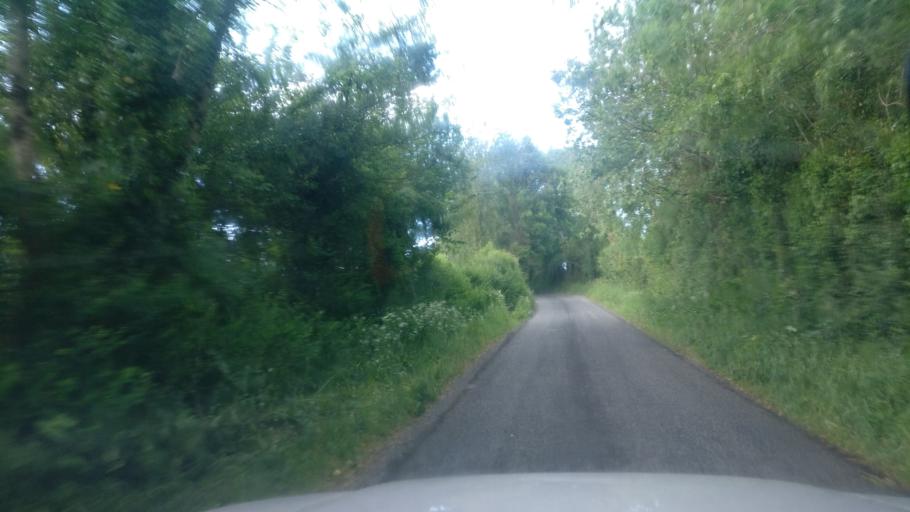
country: IE
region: Connaught
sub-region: County Galway
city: Ballinasloe
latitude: 53.2354
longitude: -8.2306
